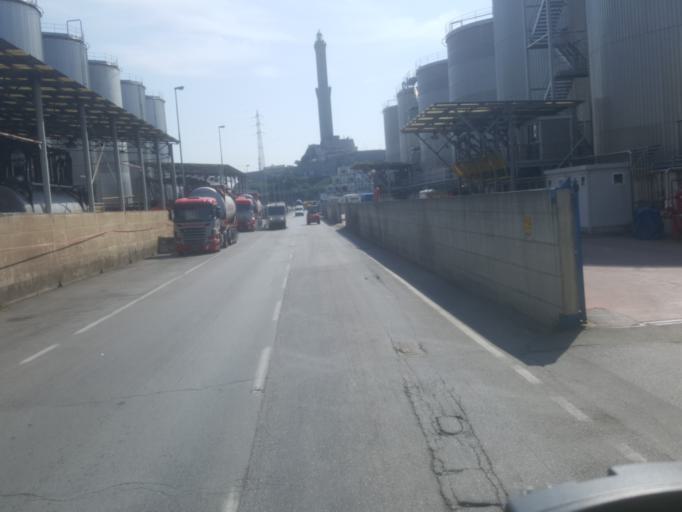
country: IT
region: Liguria
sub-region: Provincia di Genova
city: San Teodoro
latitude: 44.4058
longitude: 8.8989
